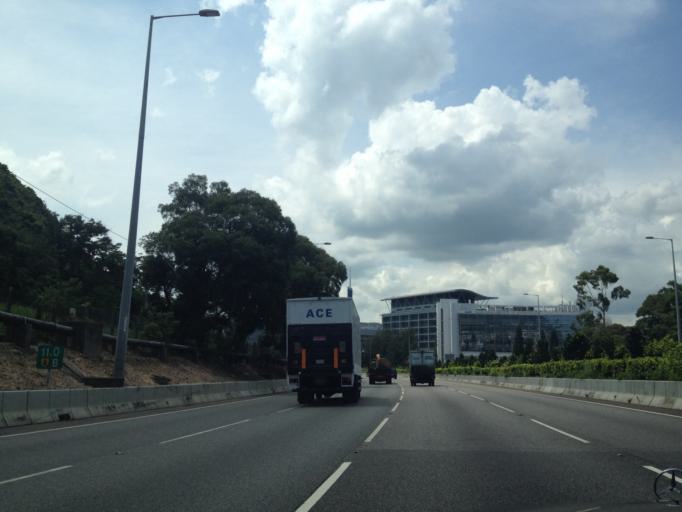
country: HK
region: Sha Tin
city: Sha Tin
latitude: 22.4201
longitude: 114.2133
